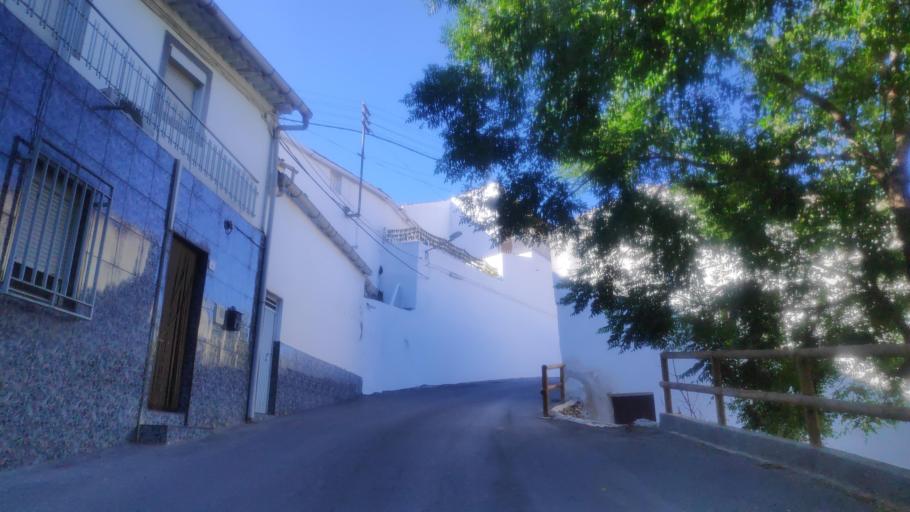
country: ES
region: Andalusia
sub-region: Provincia de Jaen
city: Pozo Alcon
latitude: 37.6730
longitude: -2.9719
